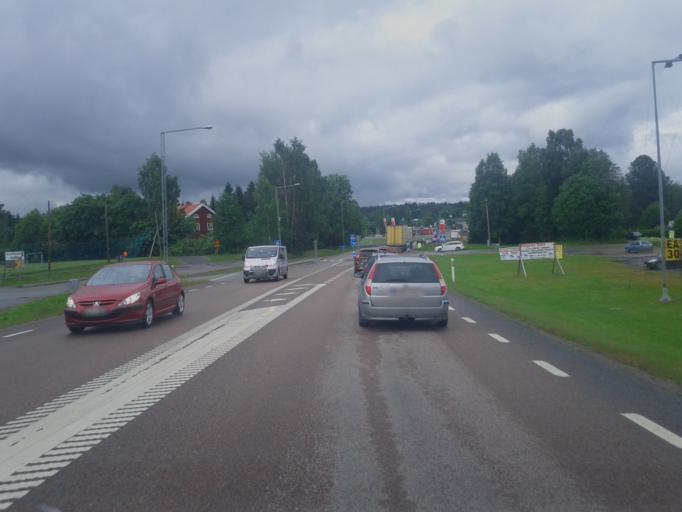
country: SE
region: Vaesternorrland
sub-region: Haernoesands Kommun
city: Haernoesand
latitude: 62.6709
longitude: 17.8402
